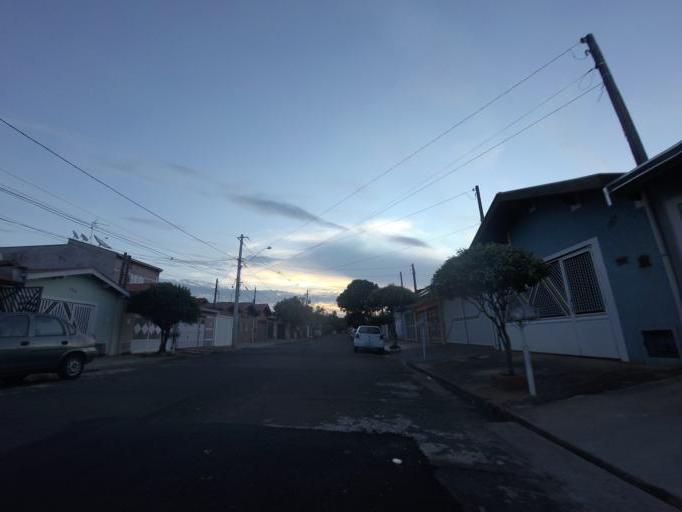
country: BR
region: Sao Paulo
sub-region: Piracicaba
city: Piracicaba
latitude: -22.7655
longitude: -47.5884
